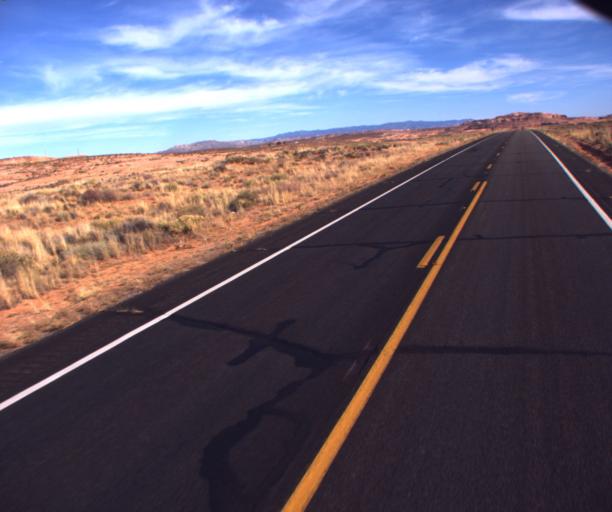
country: US
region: Arizona
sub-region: Apache County
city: Many Farms
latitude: 36.9337
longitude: -109.6300
